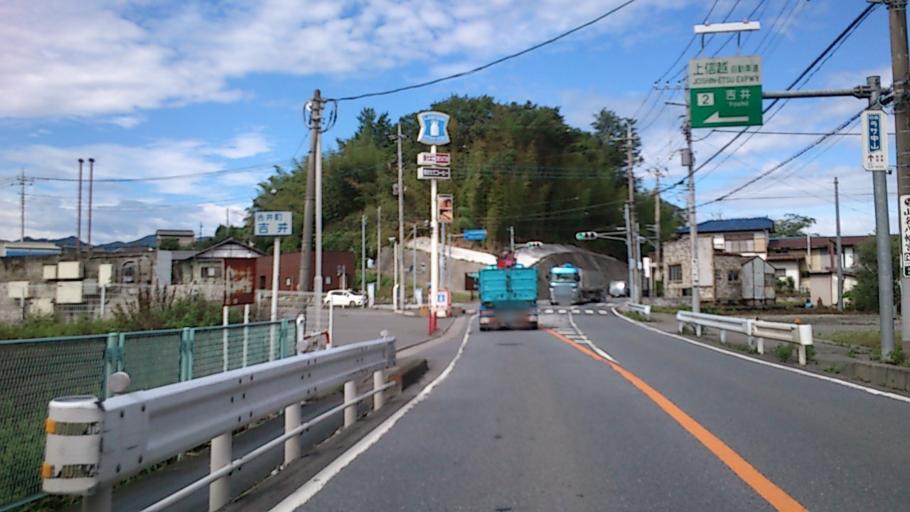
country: JP
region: Gunma
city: Yoshii
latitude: 36.2537
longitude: 138.9956
